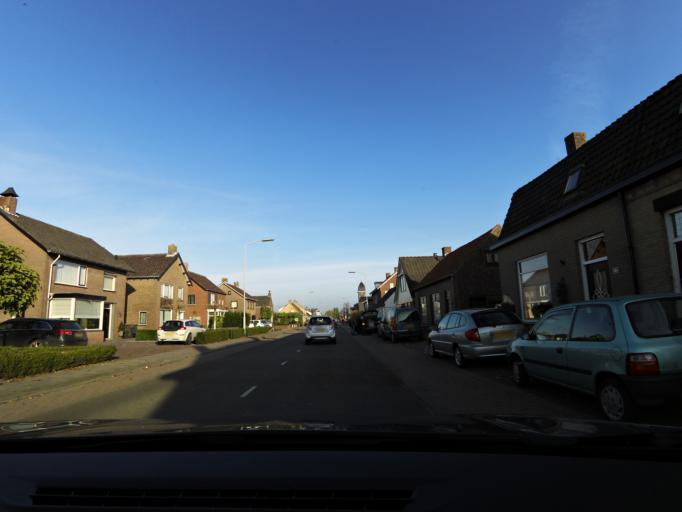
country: NL
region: North Brabant
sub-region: Gemeente Made en Drimmelen
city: Made
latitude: 51.6734
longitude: 4.7794
